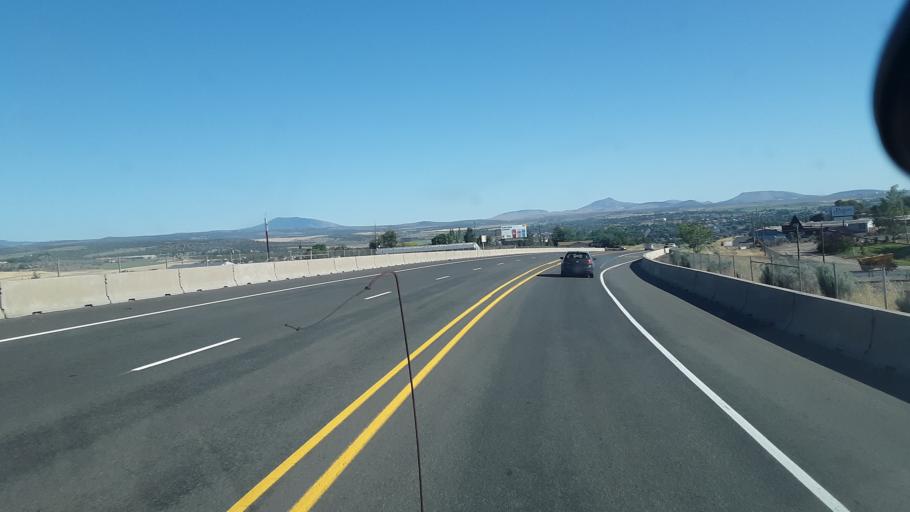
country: US
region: Oregon
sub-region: Jefferson County
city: Madras
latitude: 44.6540
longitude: -121.1293
